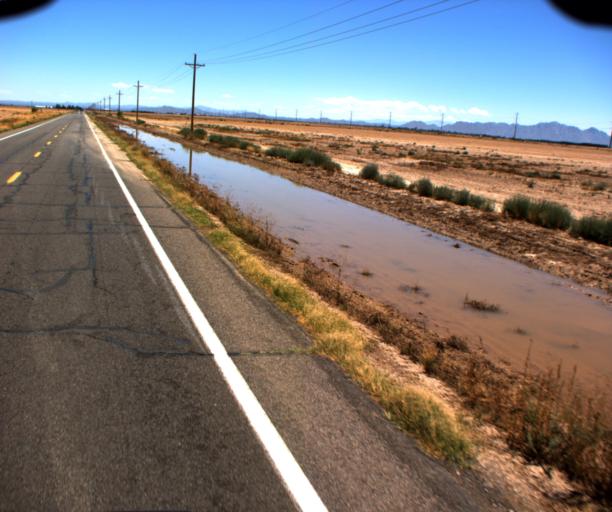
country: US
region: Arizona
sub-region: Pinal County
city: Coolidge
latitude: 32.8797
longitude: -111.6099
